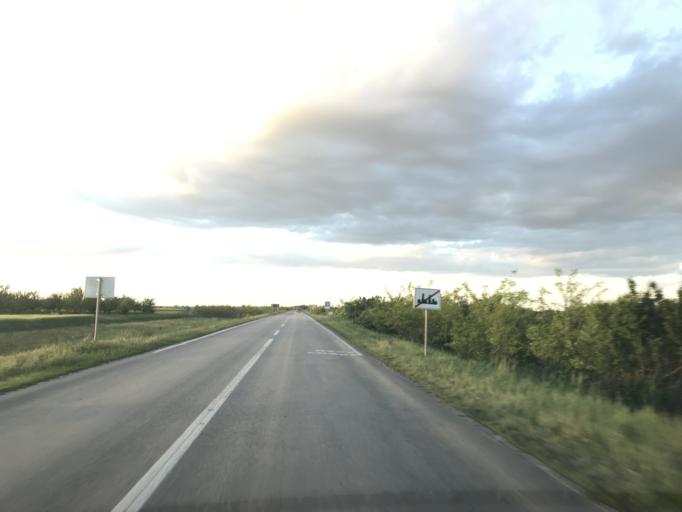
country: RS
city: Banatsko Karadordevo
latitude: 45.5968
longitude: 20.5609
